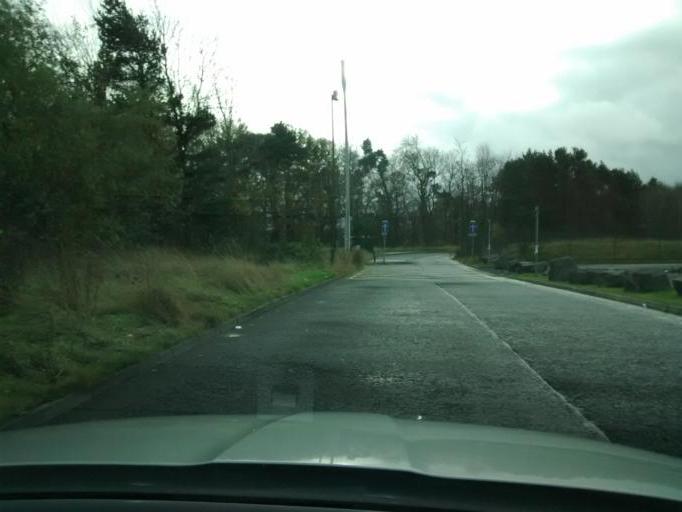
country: GB
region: Scotland
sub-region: West Lothian
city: West Calder
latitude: 55.8803
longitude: -3.5496
